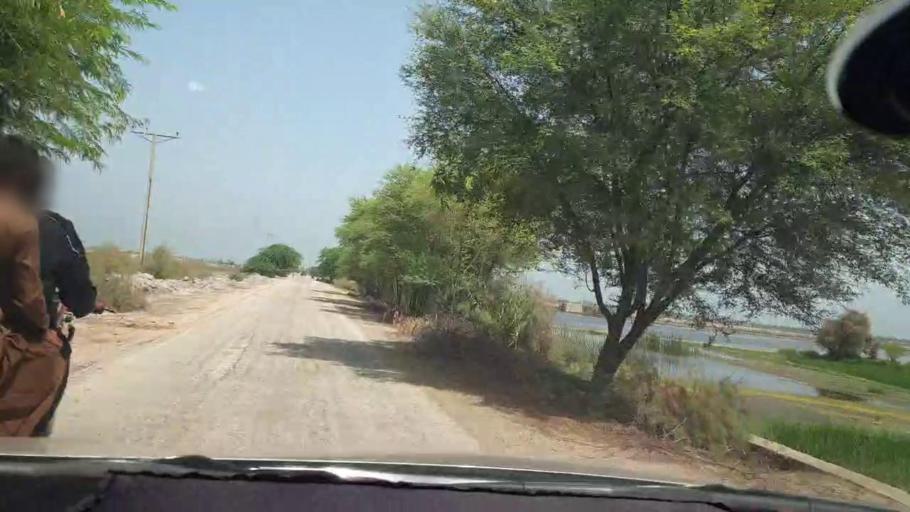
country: PK
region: Sindh
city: Kambar
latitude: 27.6816
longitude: 67.9192
